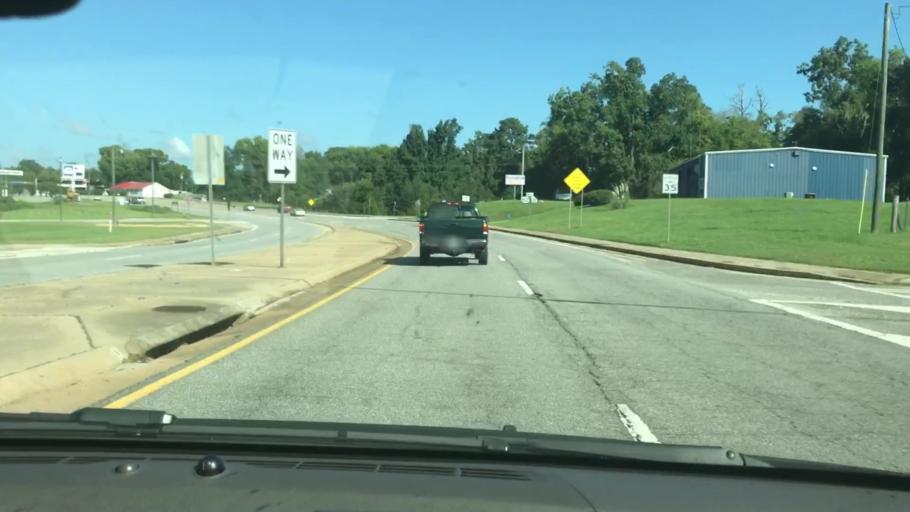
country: US
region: Georgia
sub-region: Quitman County
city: Georgetown
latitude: 31.8863
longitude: -85.1060
